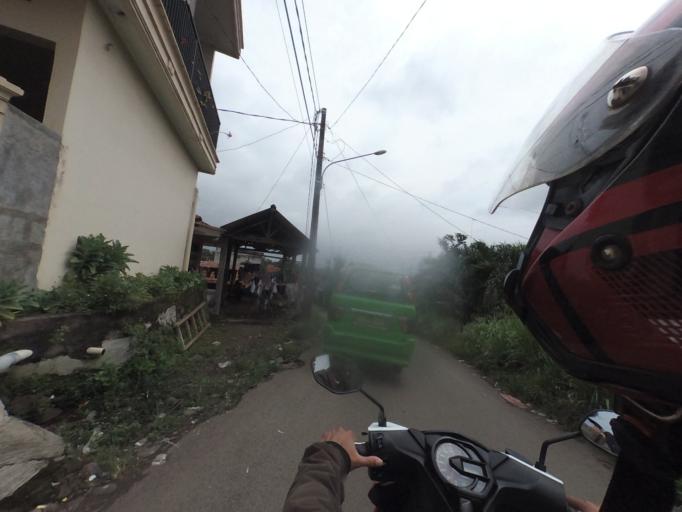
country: ID
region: West Java
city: Bogor
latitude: -6.6079
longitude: 106.7578
